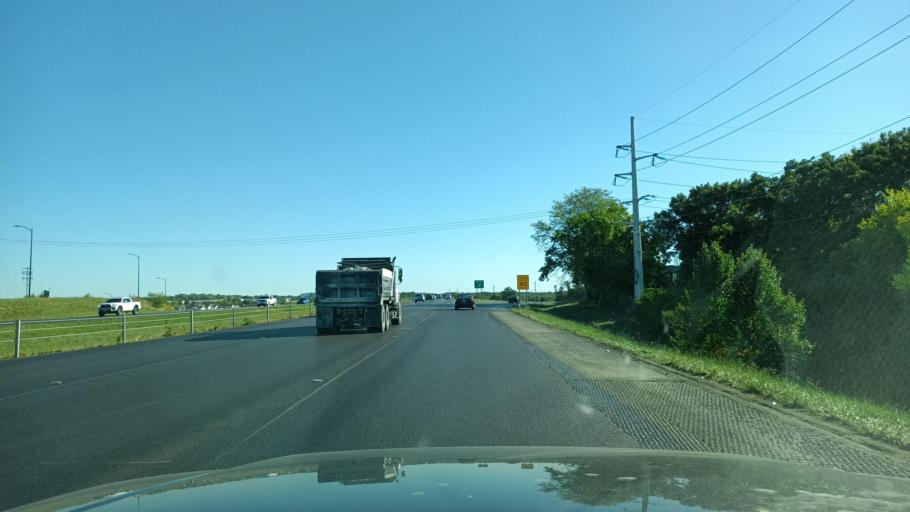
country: US
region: Missouri
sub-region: Boone County
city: Columbia
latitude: 38.9365
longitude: -92.2951
